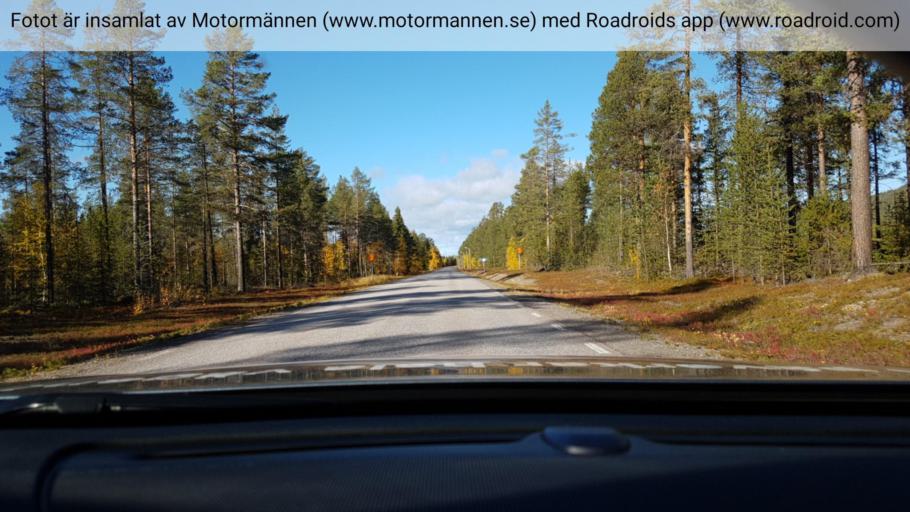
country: SE
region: Norrbotten
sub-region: Arvidsjaurs Kommun
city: Arvidsjaur
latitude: 65.6815
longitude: 18.8154
